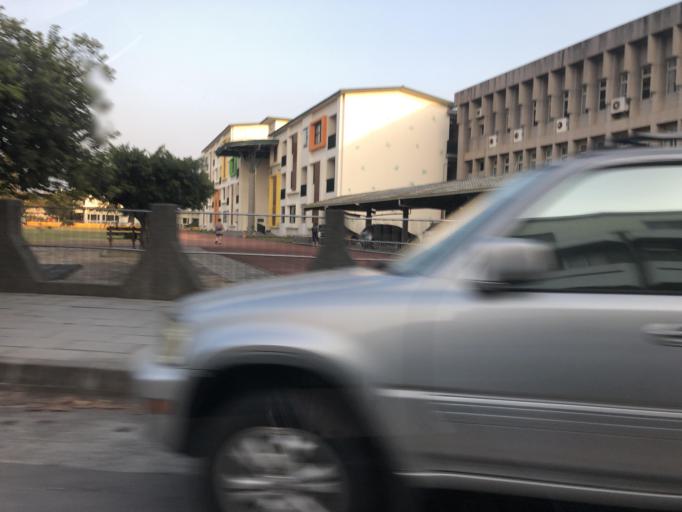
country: TW
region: Taiwan
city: Xinying
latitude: 23.1865
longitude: 120.2530
